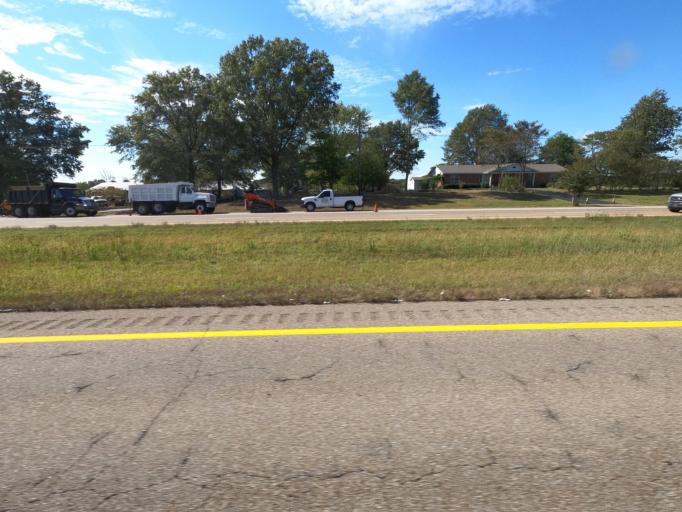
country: US
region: Tennessee
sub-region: Crockett County
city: Alamo
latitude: 35.8480
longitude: -89.1939
